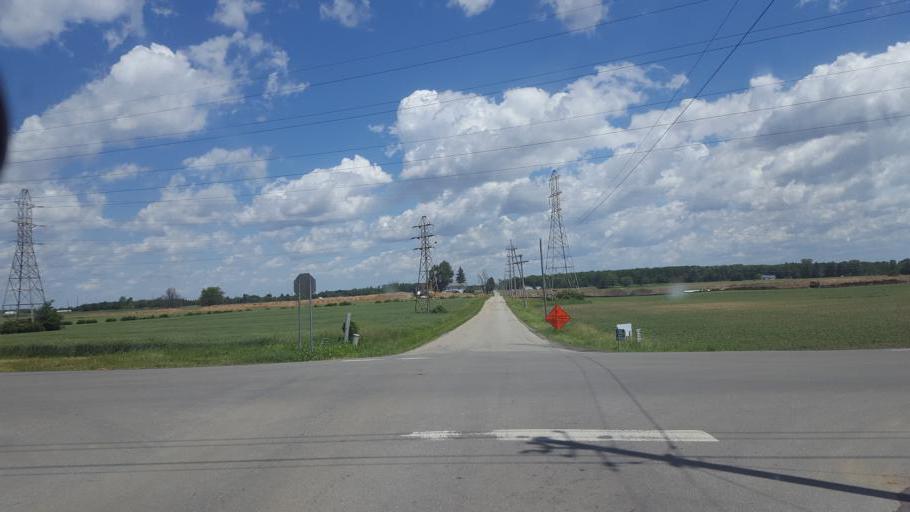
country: US
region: Ohio
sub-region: Richland County
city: Shelby
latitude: 40.8500
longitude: -82.6773
